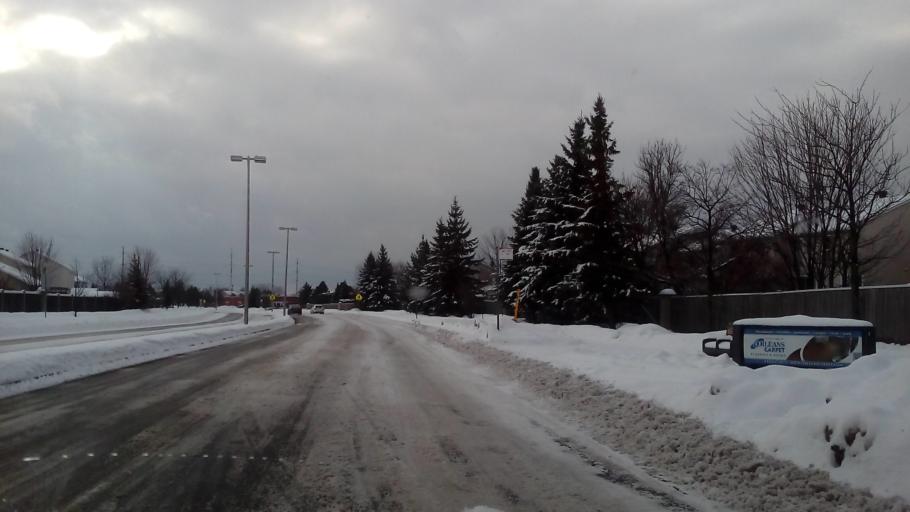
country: CA
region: Ontario
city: Clarence-Rockland
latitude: 45.4744
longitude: -75.4698
